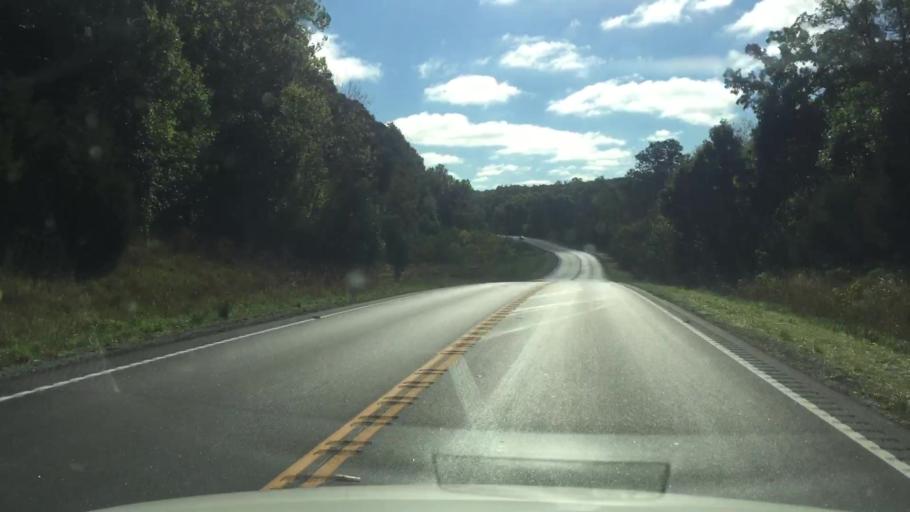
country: US
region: Missouri
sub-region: Howard County
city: New Franklin
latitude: 38.9892
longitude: -92.5584
